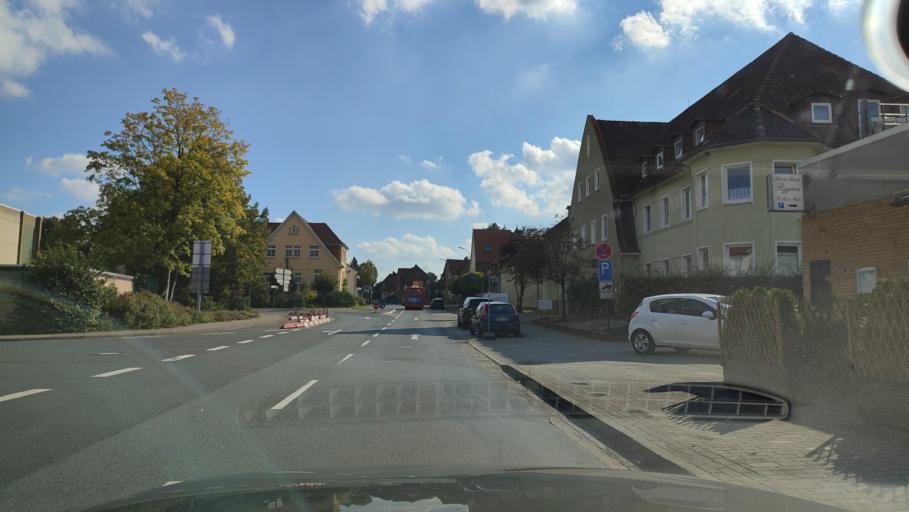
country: DE
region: Lower Saxony
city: Bomlitz
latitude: 52.9047
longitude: 9.6581
